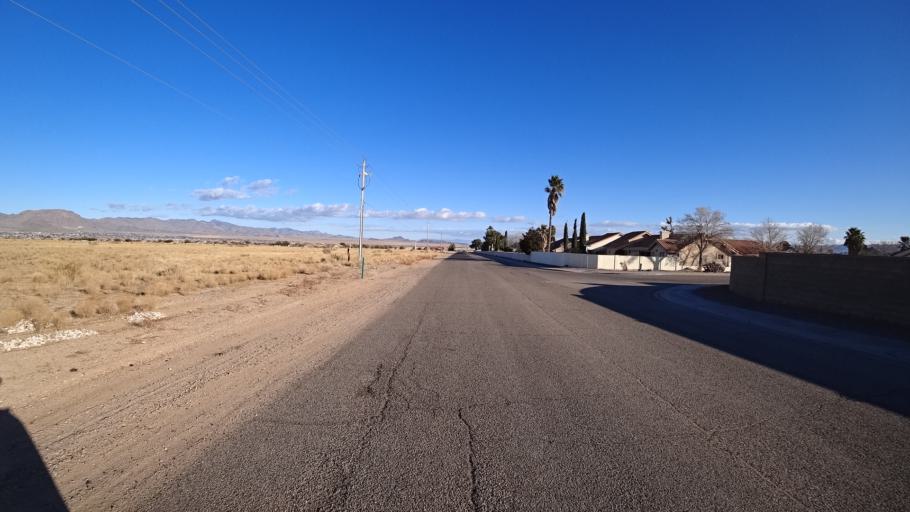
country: US
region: Arizona
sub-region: Mohave County
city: New Kingman-Butler
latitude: 35.2208
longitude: -113.9761
